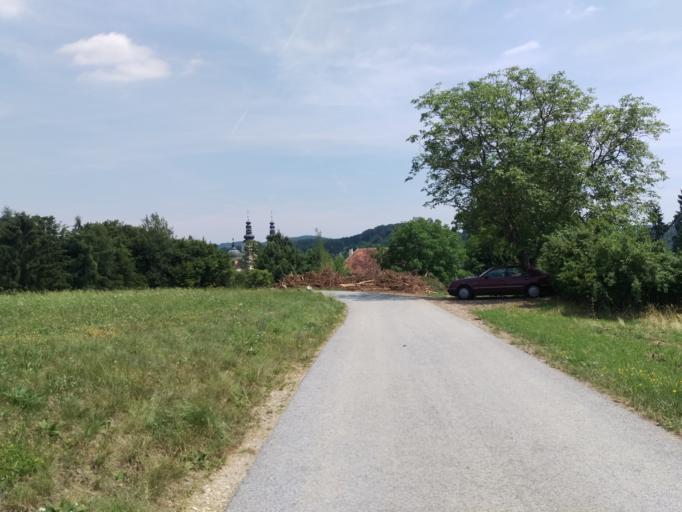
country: AT
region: Styria
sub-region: Graz Stadt
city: Mariatrost
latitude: 47.1083
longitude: 15.4859
